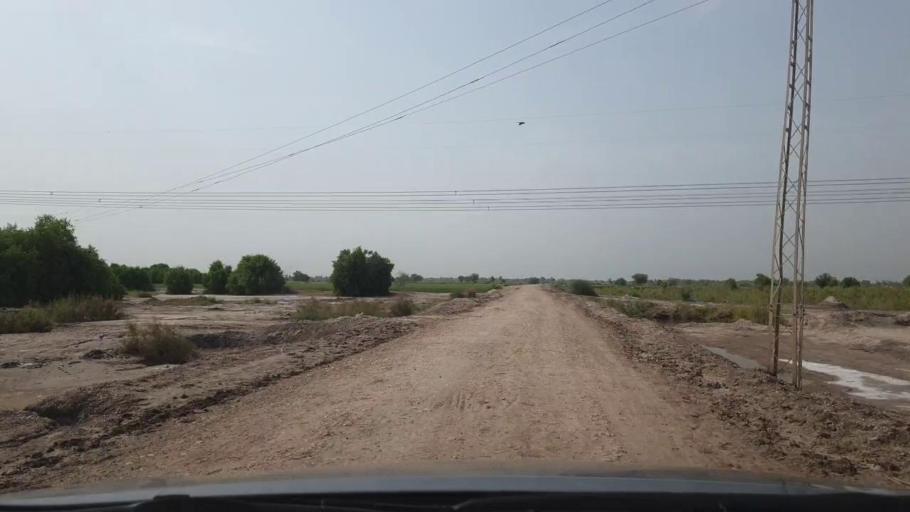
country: PK
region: Sindh
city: Rohri
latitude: 27.6749
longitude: 69.0124
